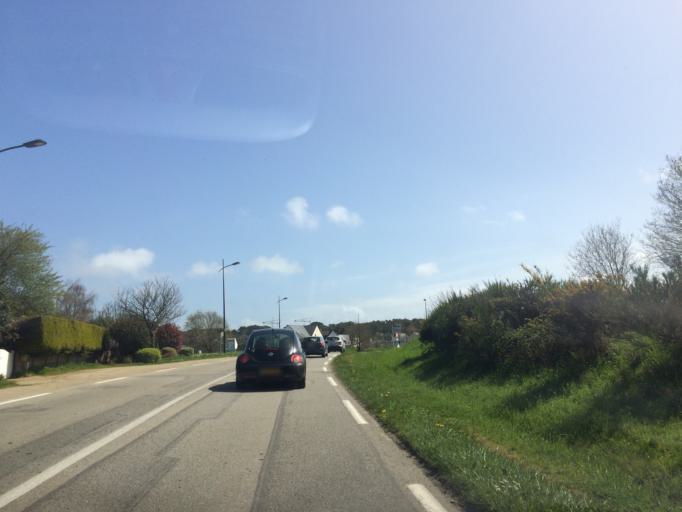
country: FR
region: Brittany
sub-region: Departement du Morbihan
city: La Trinite-sur-Mer
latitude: 47.5953
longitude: -3.0372
